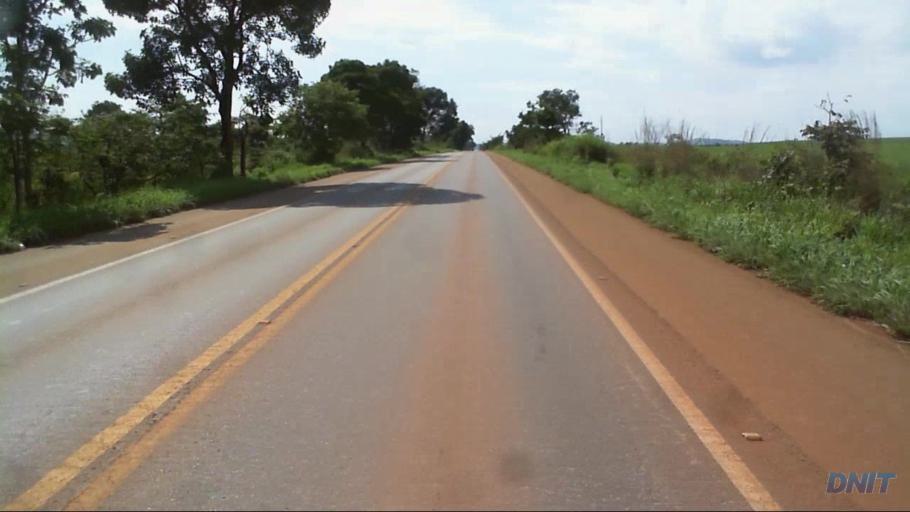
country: BR
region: Goias
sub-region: Barro Alto
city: Barro Alto
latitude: -15.0563
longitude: -48.8803
